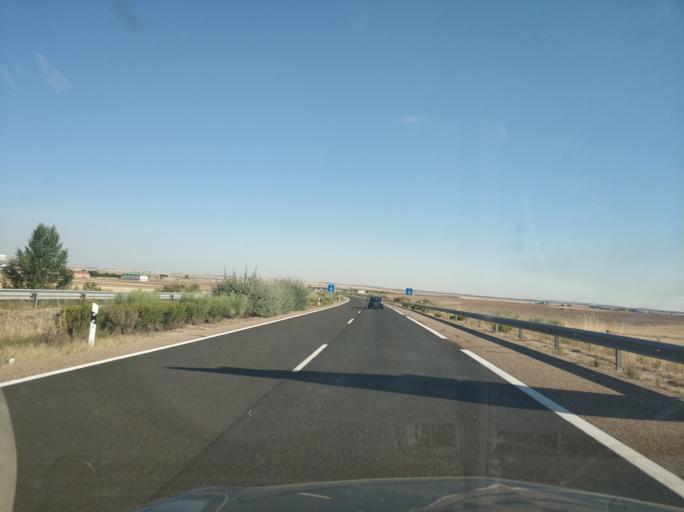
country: ES
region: Castille and Leon
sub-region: Provincia de Salamanca
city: Pajares de la Laguna
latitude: 41.0841
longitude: -5.5045
